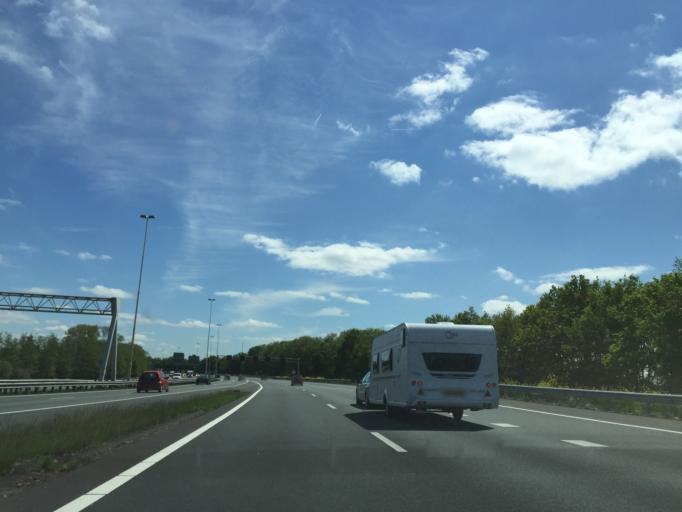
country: NL
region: Utrecht
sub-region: Gemeente Leusden
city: Leusden
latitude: 52.1694
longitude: 5.4407
